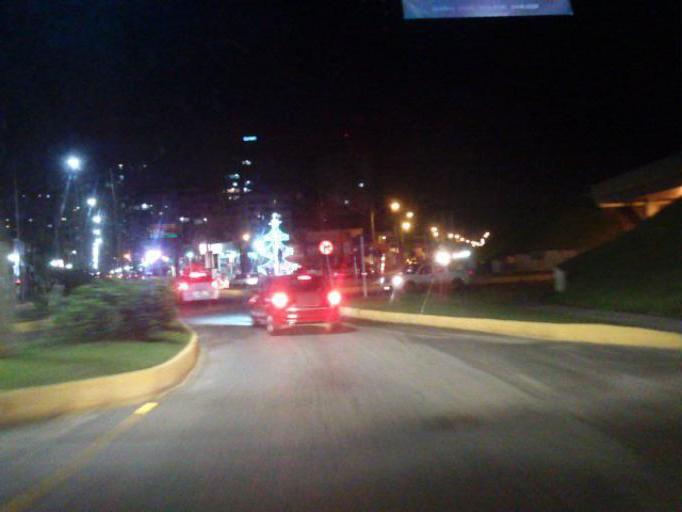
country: BR
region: Santa Catarina
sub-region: Itapema
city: Itapema
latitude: -27.1175
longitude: -48.6090
